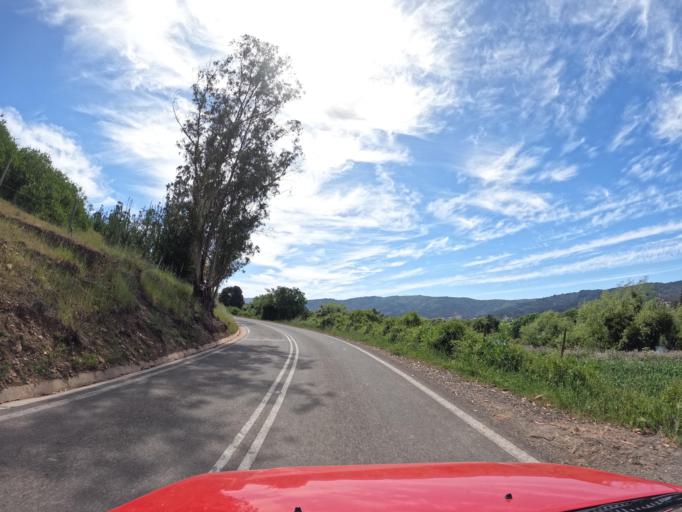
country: CL
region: Maule
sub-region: Provincia de Talca
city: Talca
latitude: -35.0061
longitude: -71.9779
